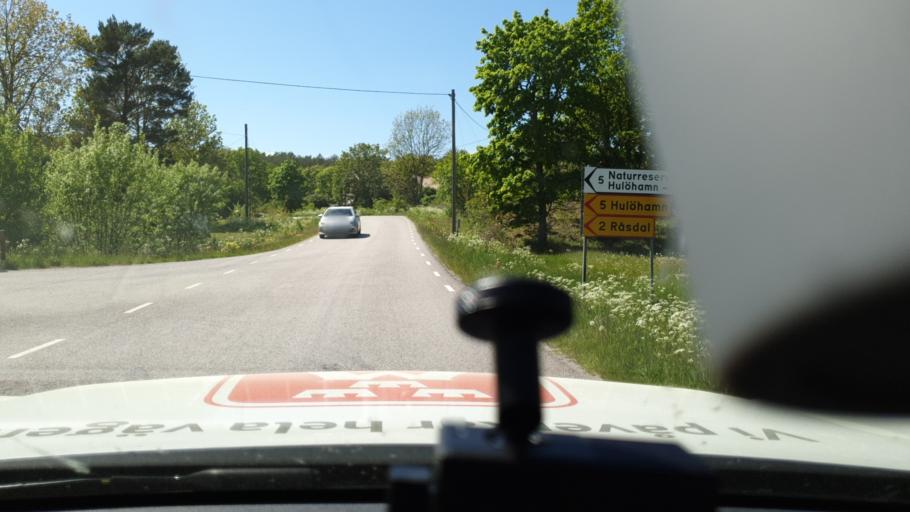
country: SE
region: Kalmar
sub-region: Vasterviks Kommun
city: Vaestervik
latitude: 57.9385
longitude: 16.7432
